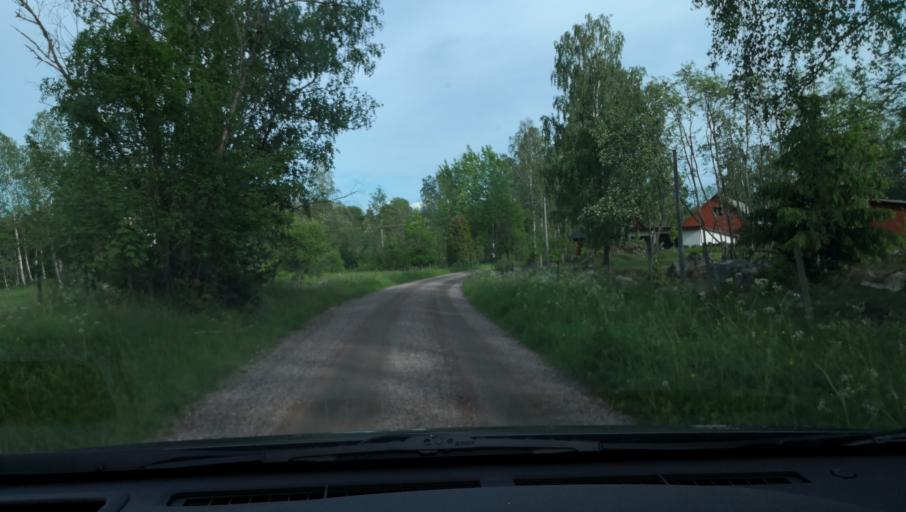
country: SE
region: Vaestmanland
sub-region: Kungsors Kommun
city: Kungsoer
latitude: 59.3630
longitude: 16.0216
